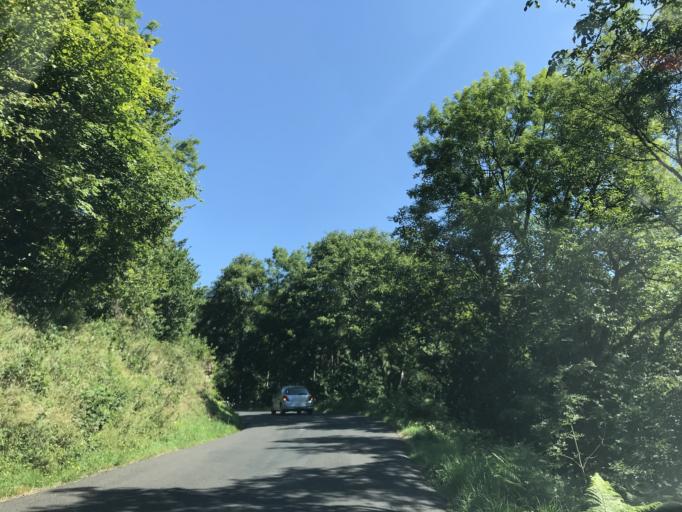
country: FR
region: Auvergne
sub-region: Departement du Puy-de-Dome
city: Job
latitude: 45.6698
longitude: 3.7292
